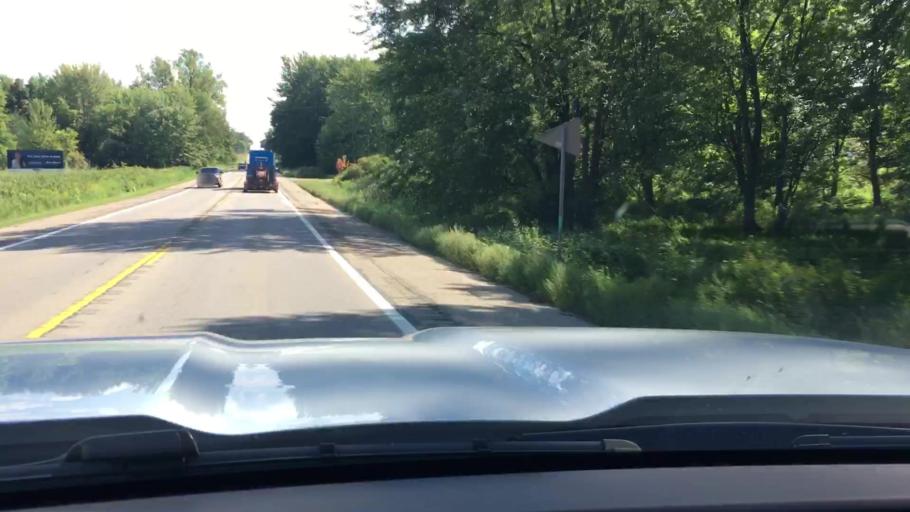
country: US
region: Michigan
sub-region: Ionia County
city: Ionia
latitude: 43.0640
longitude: -85.0752
